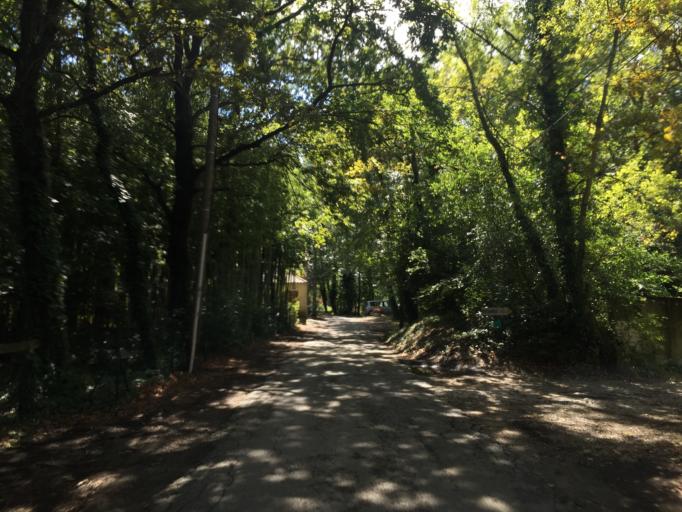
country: FR
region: Provence-Alpes-Cote d'Azur
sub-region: Departement du Vaucluse
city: Caderousse
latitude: 44.1307
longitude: 4.7317
